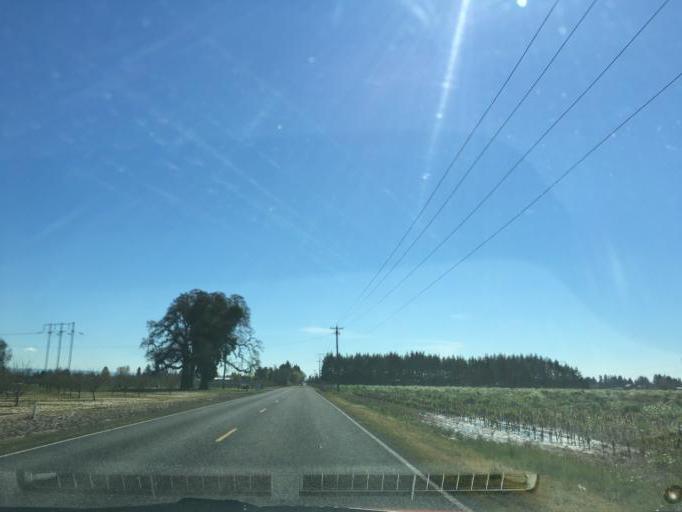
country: US
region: Oregon
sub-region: Marion County
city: Hubbard
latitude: 45.1813
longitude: -122.7226
